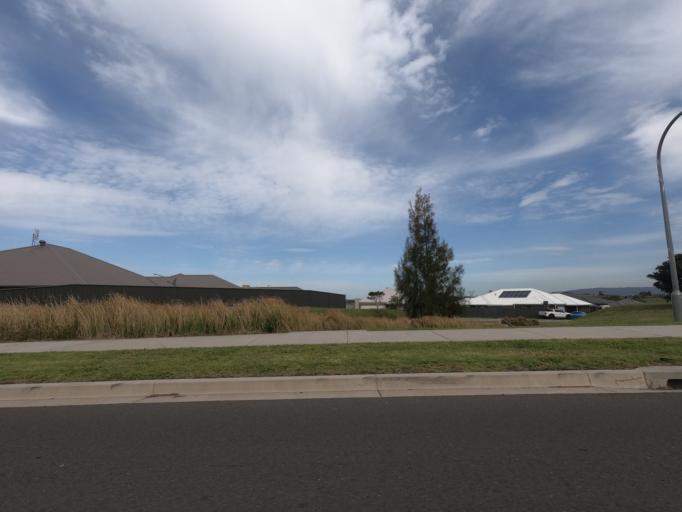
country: AU
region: New South Wales
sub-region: Wollongong
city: Dapto
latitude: -34.4941
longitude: 150.7603
